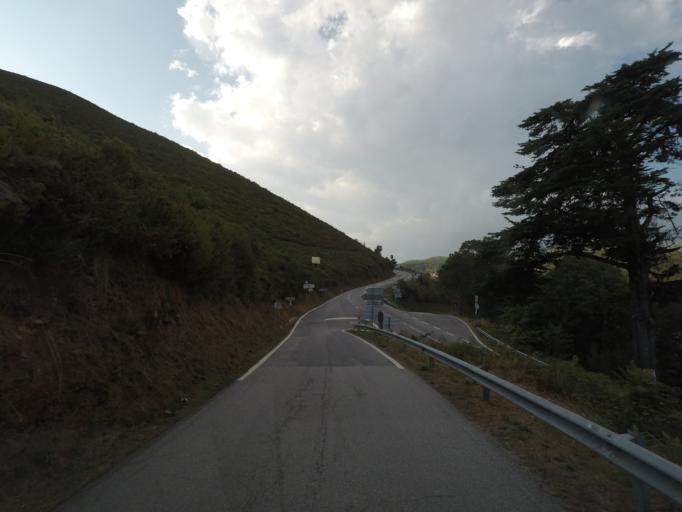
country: PT
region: Porto
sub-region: Baiao
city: Valadares
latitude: 41.1823
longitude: -7.9371
